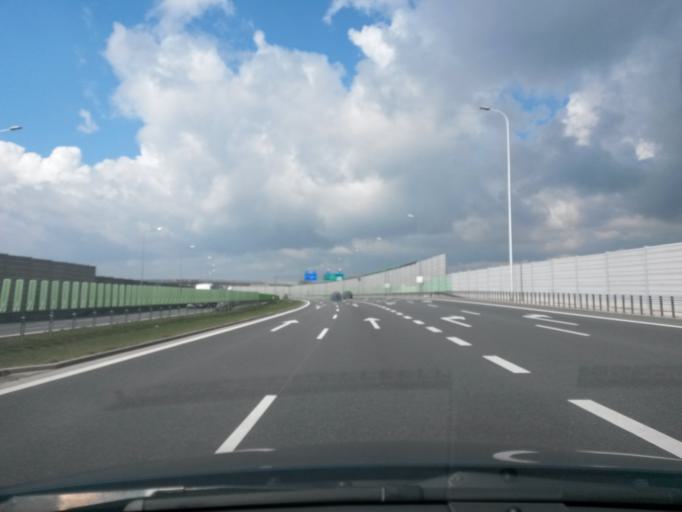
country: PL
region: Masovian Voivodeship
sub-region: Powiat pruszkowski
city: Piastow
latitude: 52.1972
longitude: 20.8518
